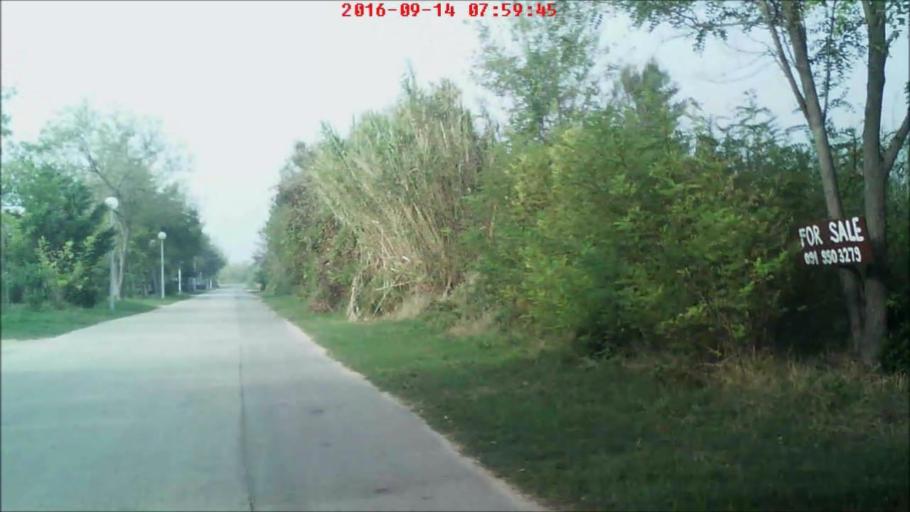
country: HR
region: Zadarska
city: Nin
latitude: 44.2583
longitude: 15.1583
